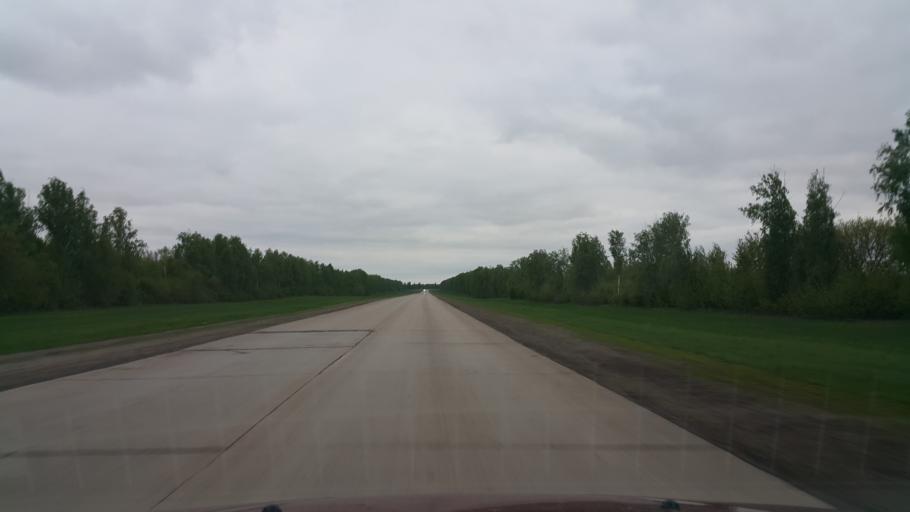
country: RU
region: Tambov
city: Znamenka
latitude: 52.3885
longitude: 41.4332
